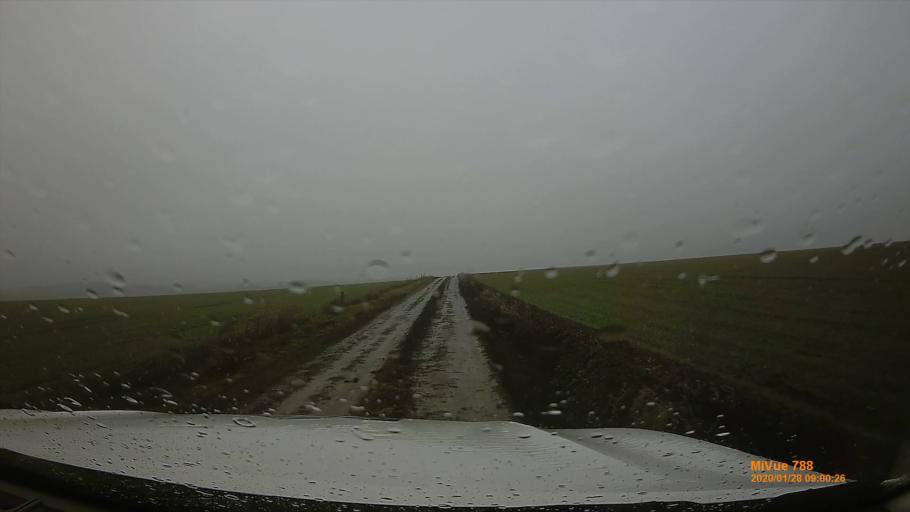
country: HU
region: Pest
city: Pilis
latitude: 47.3110
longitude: 19.5469
